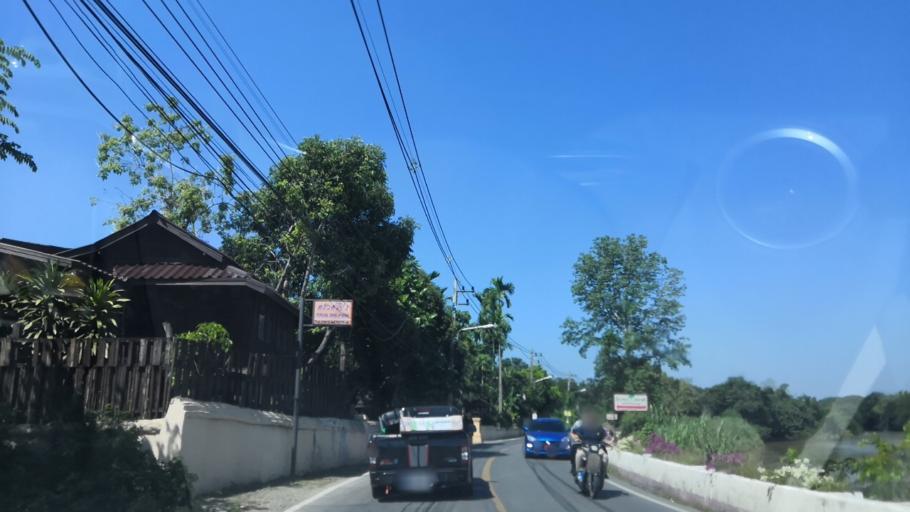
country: TH
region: Chiang Mai
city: Saraphi
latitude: 18.7290
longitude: 98.9848
